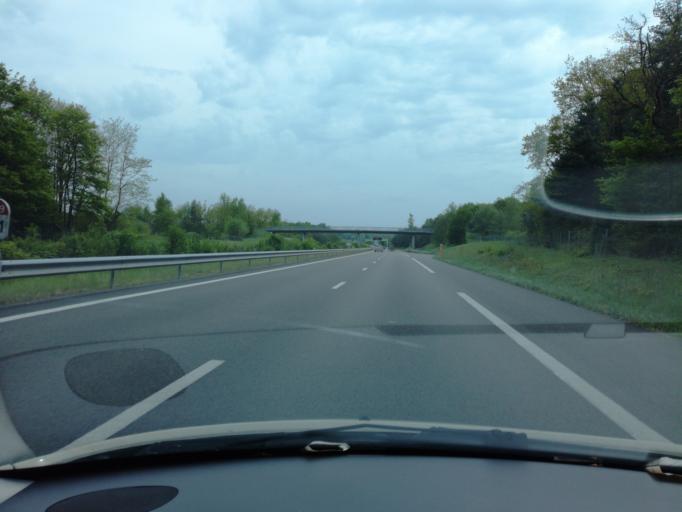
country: FR
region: Rhone-Alpes
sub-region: Departement de l'Ain
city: Viriat
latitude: 46.2832
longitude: 5.2425
